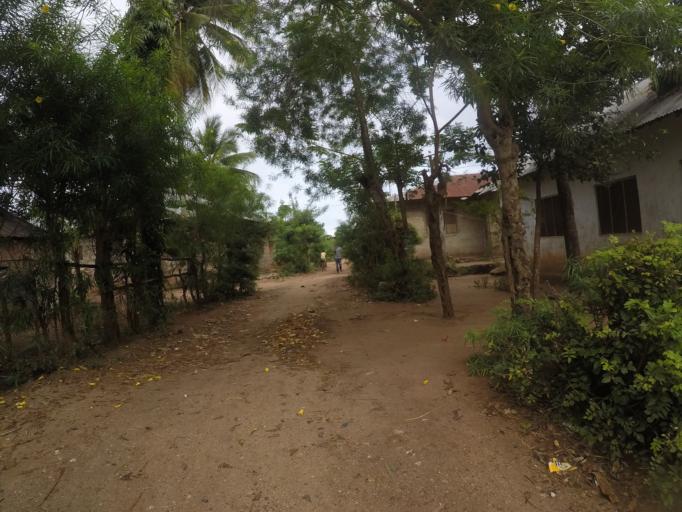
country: TZ
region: Zanzibar Urban/West
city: Zanzibar
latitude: -6.2128
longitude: 39.2163
